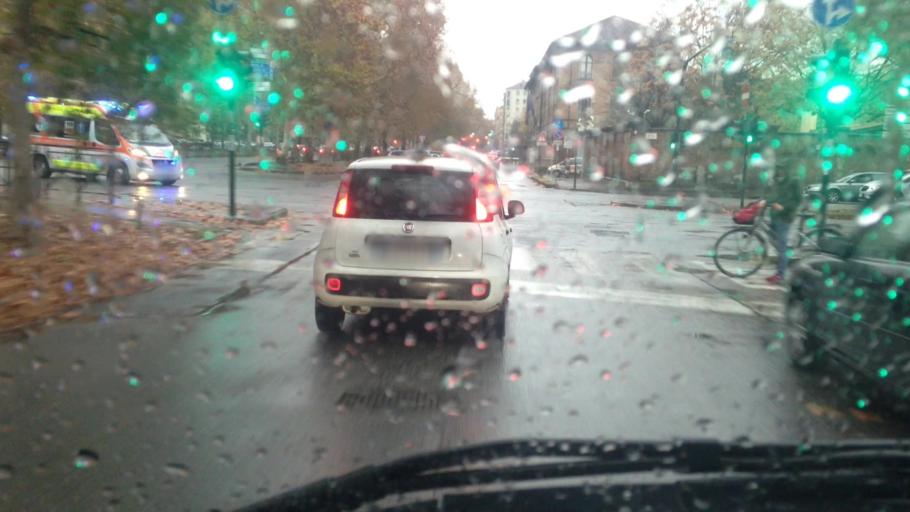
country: IT
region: Piedmont
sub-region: Provincia di Torino
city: Lesna
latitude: 45.0496
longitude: 7.6538
